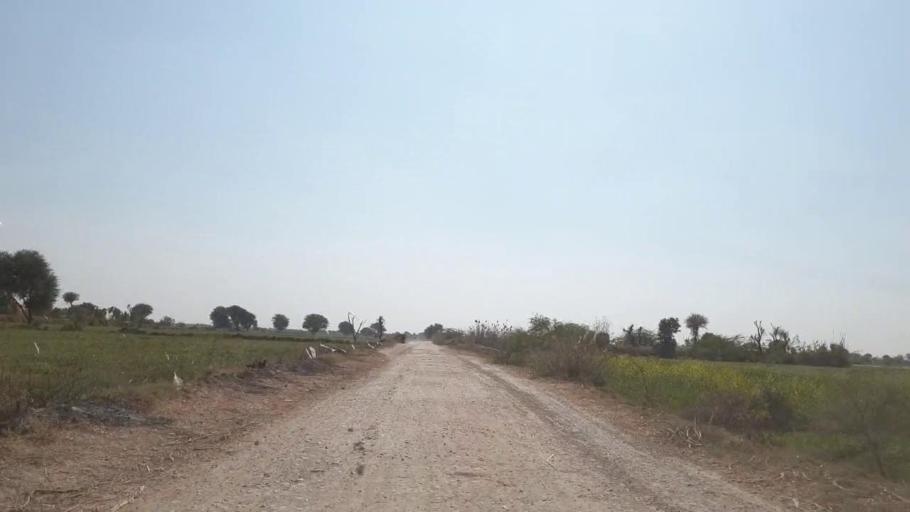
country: PK
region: Sindh
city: Mirpur Khas
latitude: 25.7388
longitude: 69.0823
